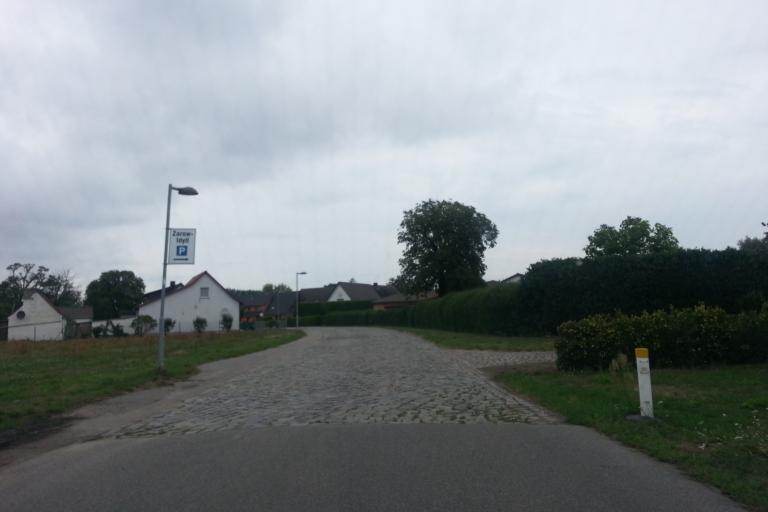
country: DE
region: Mecklenburg-Vorpommern
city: Ferdinandshof
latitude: 53.6927
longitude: 13.8942
